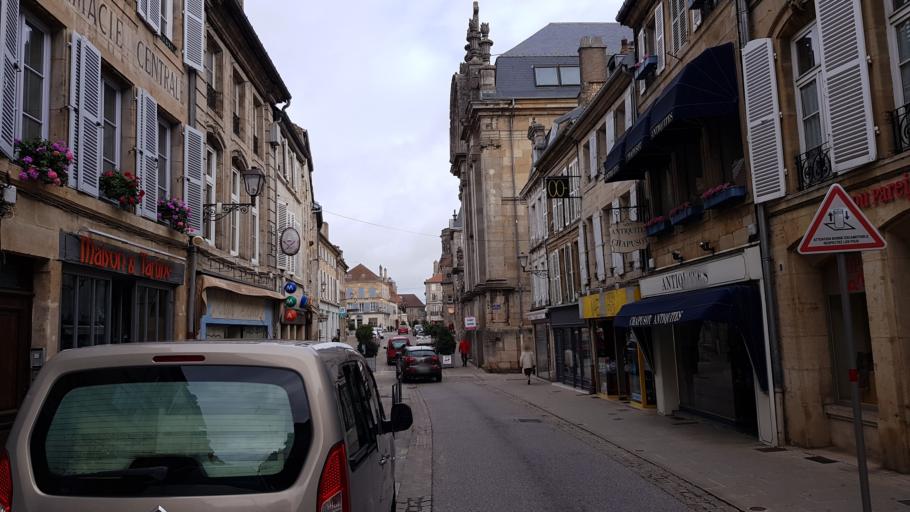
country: FR
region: Champagne-Ardenne
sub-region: Departement de la Haute-Marne
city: Langres
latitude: 47.8615
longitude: 5.3338
